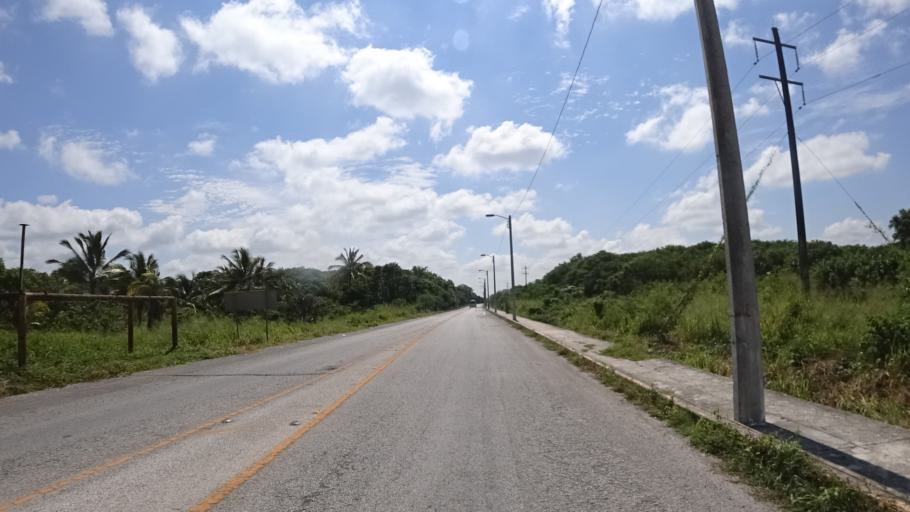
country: MX
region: Campeche
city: Sabancuy
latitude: 18.9889
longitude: -91.1907
